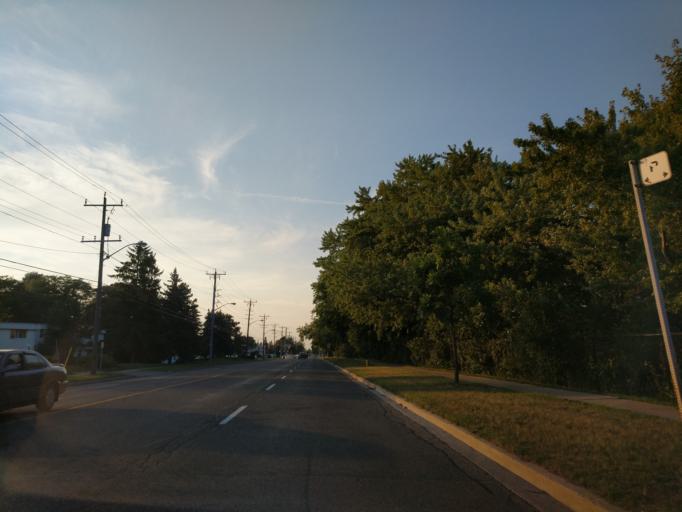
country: CA
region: Ontario
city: Scarborough
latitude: 43.7881
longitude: -79.3012
